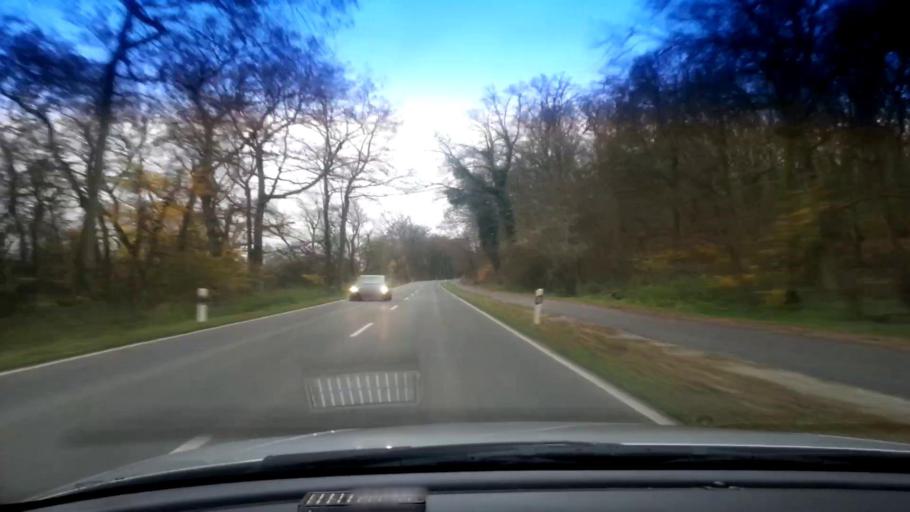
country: DE
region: Bavaria
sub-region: Upper Franconia
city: Pettstadt
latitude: 49.8563
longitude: 10.9223
